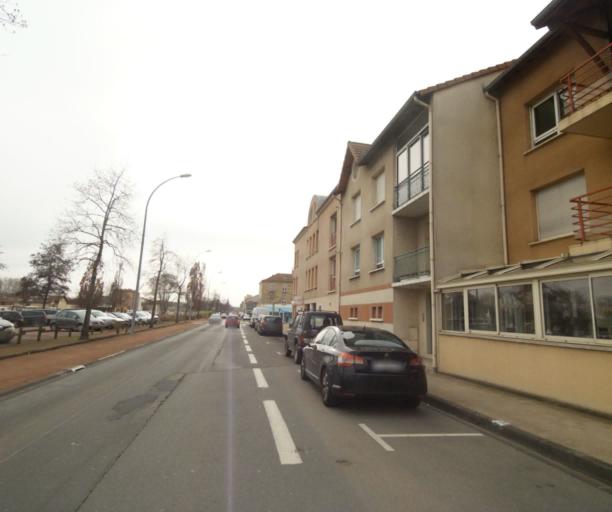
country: FR
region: Rhone-Alpes
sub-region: Departement de la Loire
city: Le Coteau
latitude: 46.0396
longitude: 4.0824
